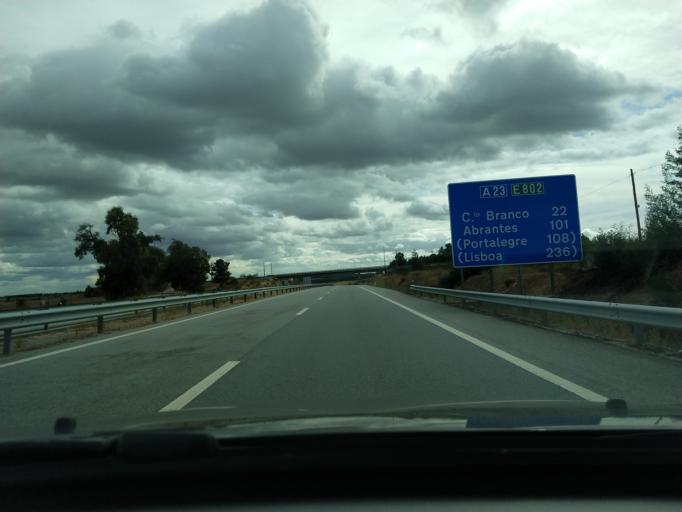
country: PT
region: Guarda
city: Alcains
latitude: 40.0194
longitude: -7.4661
